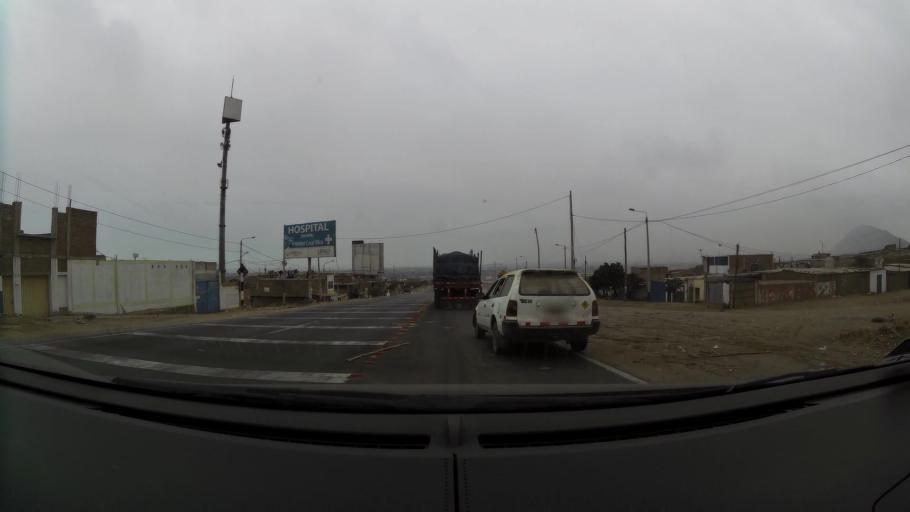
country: PE
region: La Libertad
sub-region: Provincia de Trujillo
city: Moche
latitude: -8.1830
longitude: -78.9865
